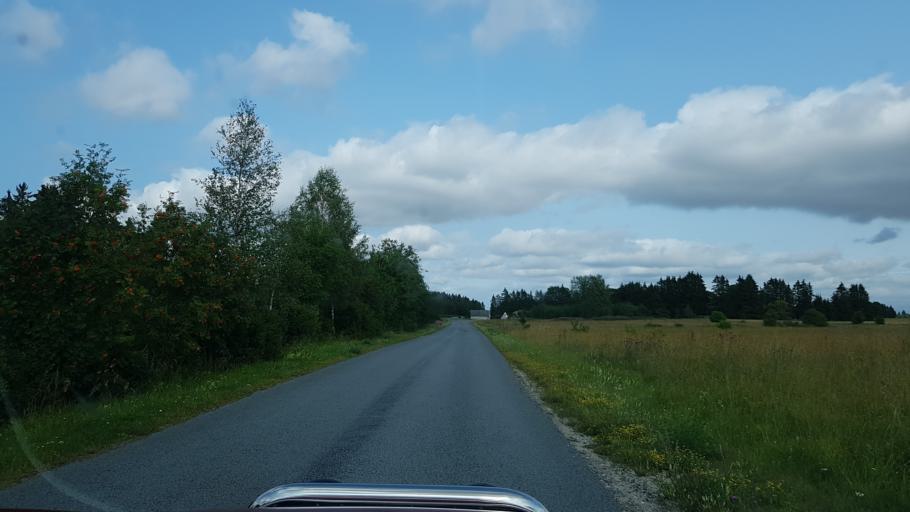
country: EE
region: Laeaene-Virumaa
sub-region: Tapa vald
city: Tapa
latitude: 59.3304
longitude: 26.0375
